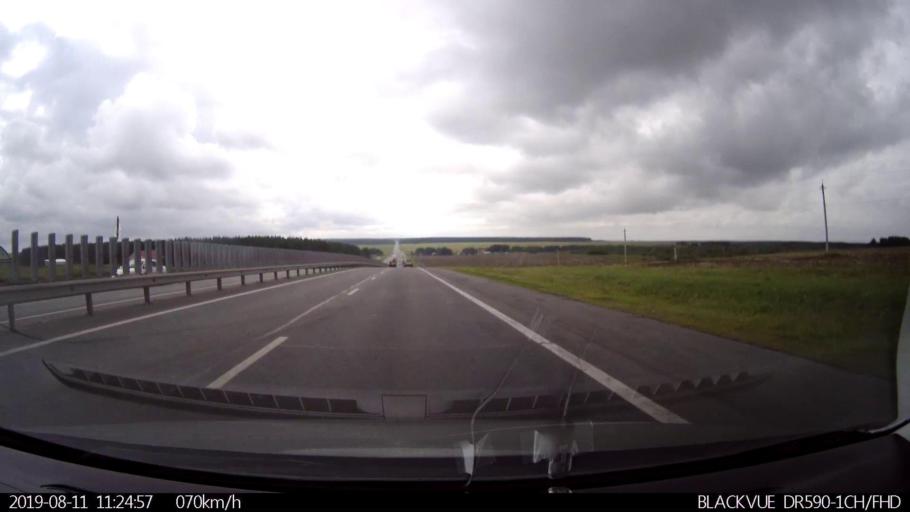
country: RU
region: Ulyanovsk
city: Krasnyy Gulyay
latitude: 54.1224
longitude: 48.2397
